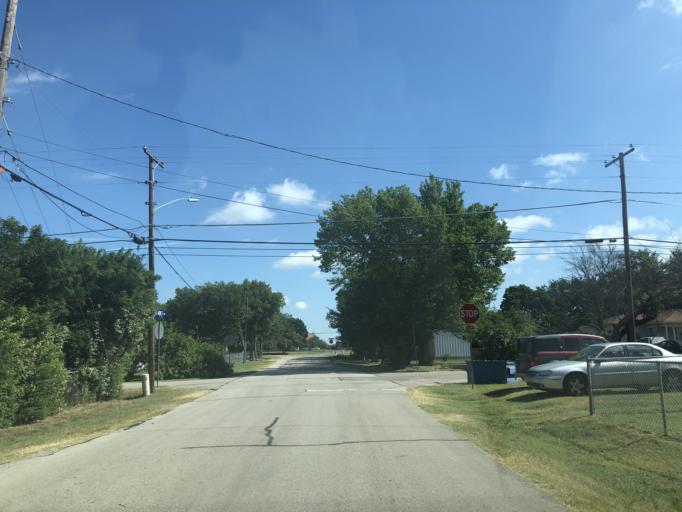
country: US
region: Texas
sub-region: Dallas County
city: Duncanville
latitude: 32.6448
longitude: -96.9099
